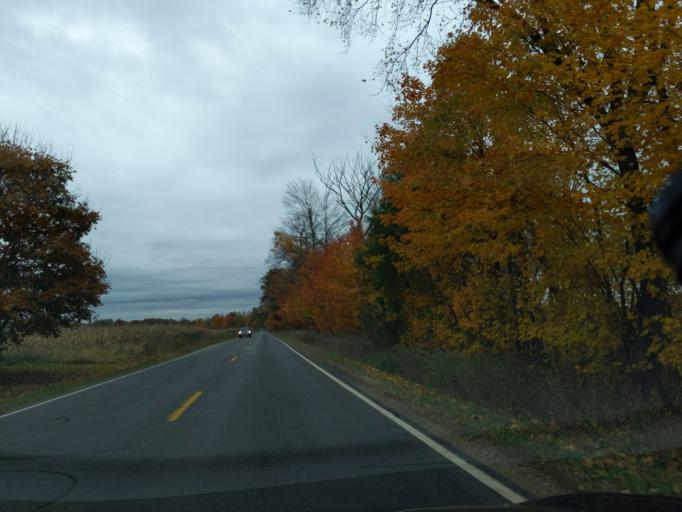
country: US
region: Michigan
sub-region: Jackson County
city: Spring Arbor
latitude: 42.3127
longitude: -84.6003
